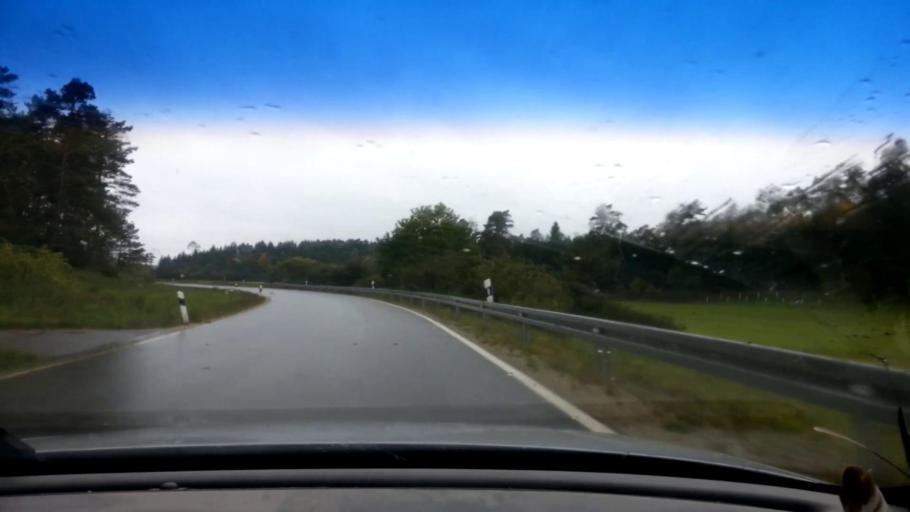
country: DE
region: Bavaria
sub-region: Upper Franconia
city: Poxdorf
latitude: 49.9426
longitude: 11.1367
